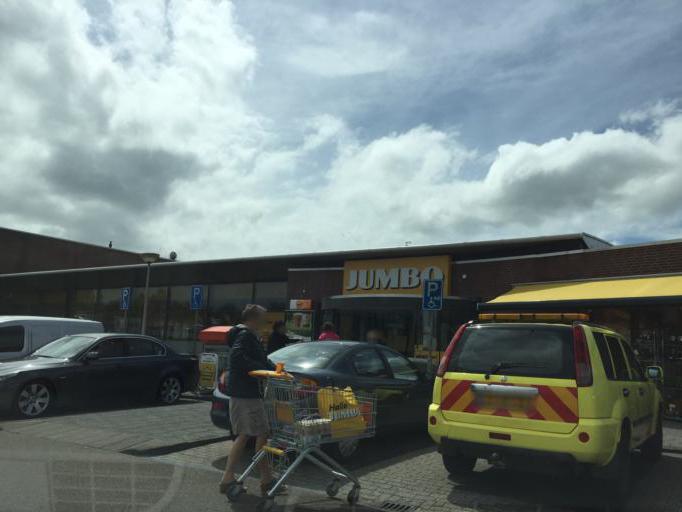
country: NL
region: Friesland
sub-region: Gemeente Dongeradeel
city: Dokkum
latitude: 53.3295
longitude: 5.9986
